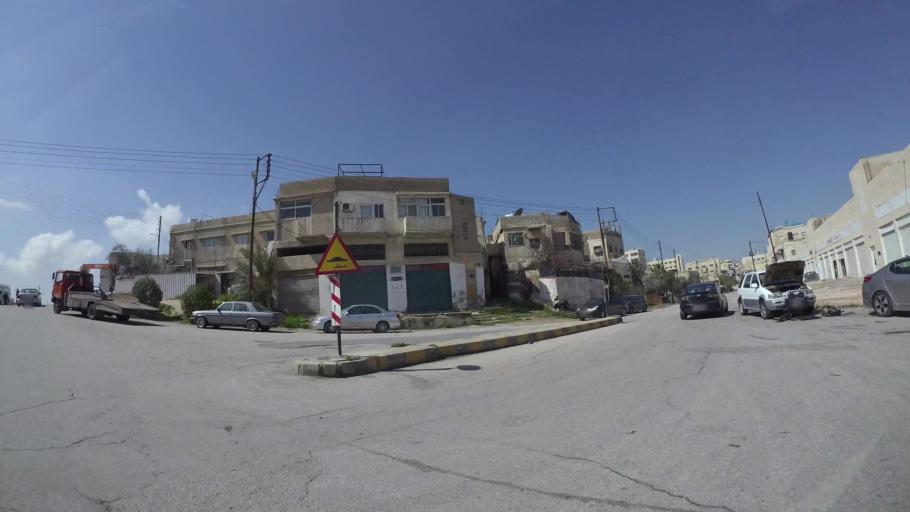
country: JO
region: Zarqa
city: Russeifa
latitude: 31.9818
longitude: 35.9999
